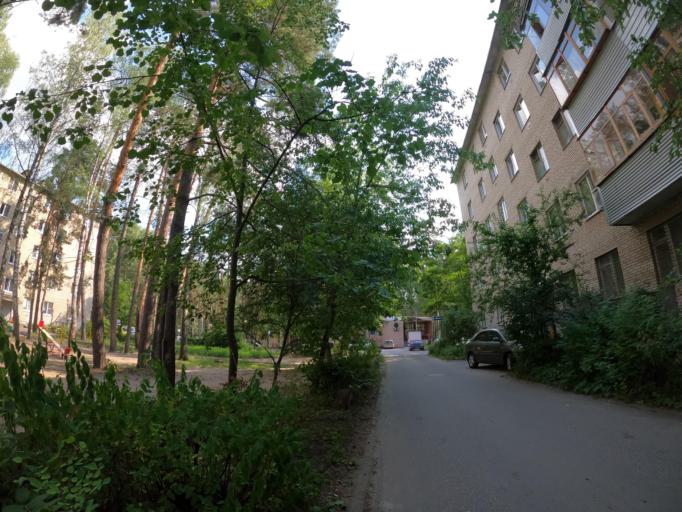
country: RU
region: Moskovskaya
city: Protvino
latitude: 54.8658
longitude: 37.2178
